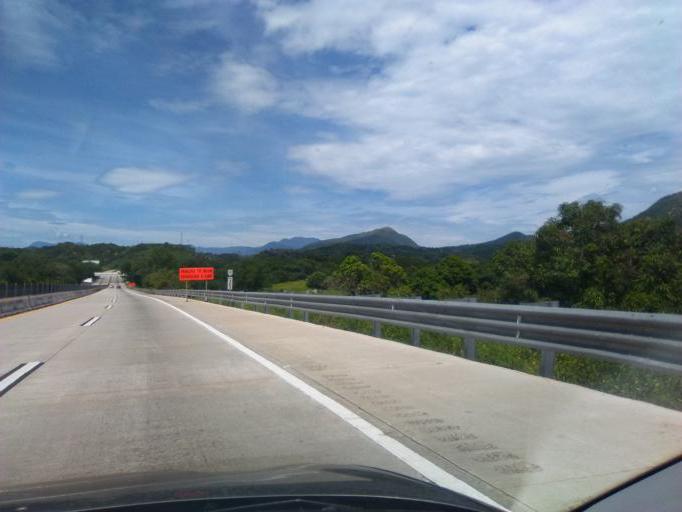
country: MX
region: Guerrero
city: Tierra Colorada
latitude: 17.1610
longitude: -99.5528
